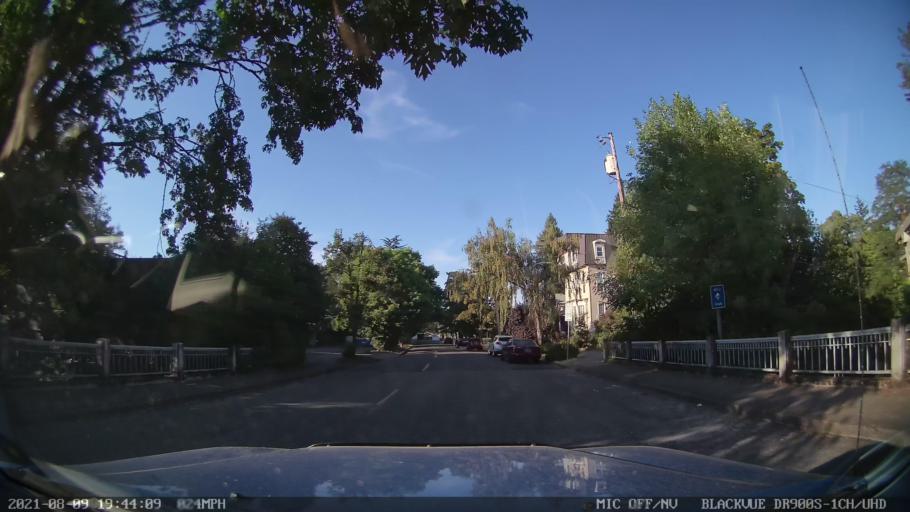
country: US
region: Oregon
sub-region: Marion County
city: Salem
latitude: 44.9461
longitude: -123.0320
